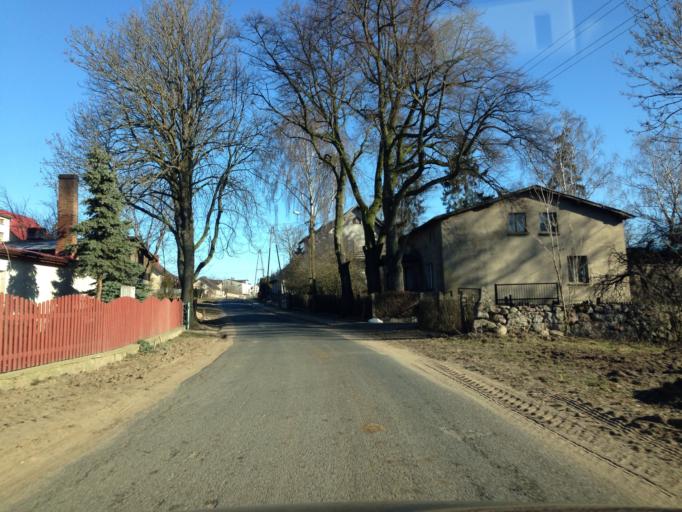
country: PL
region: Kujawsko-Pomorskie
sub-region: Powiat brodnicki
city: Brzozie
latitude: 53.3695
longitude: 19.6275
